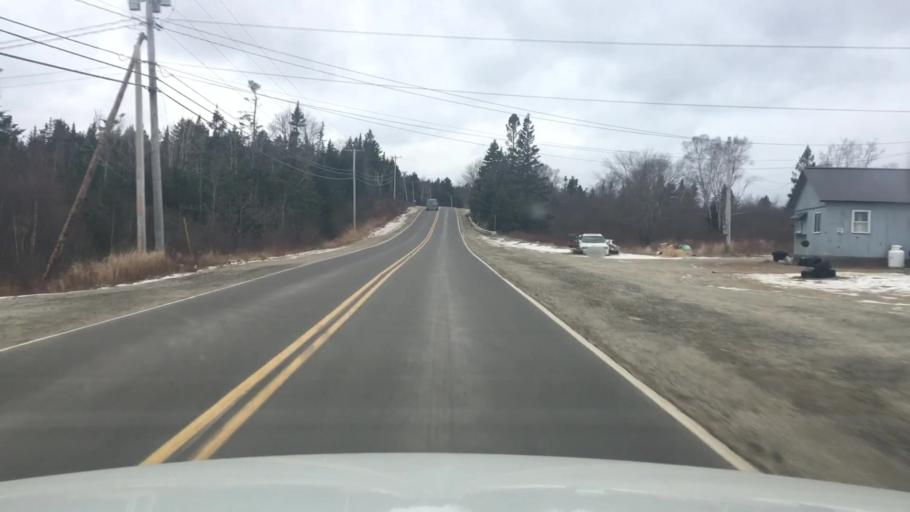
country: US
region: Maine
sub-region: Washington County
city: Jonesport
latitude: 44.5587
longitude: -67.6293
